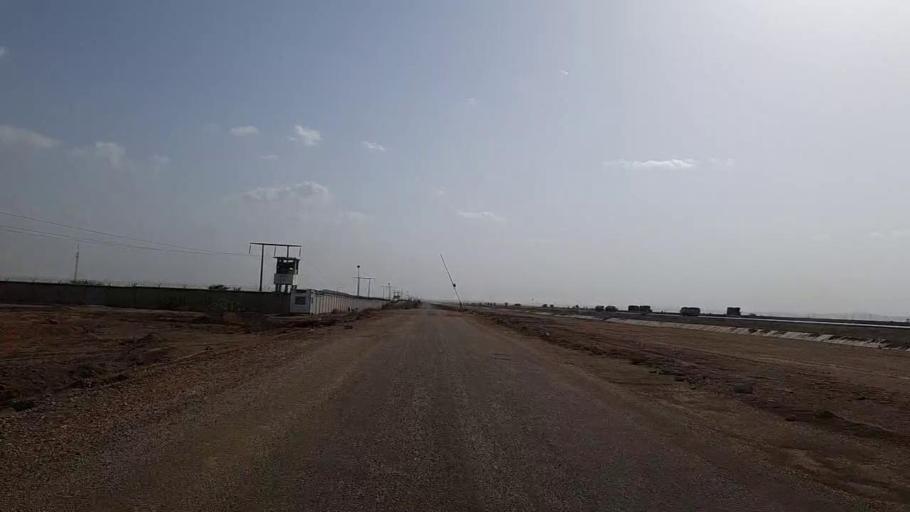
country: PK
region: Sindh
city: Kotri
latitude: 25.2890
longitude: 68.0461
